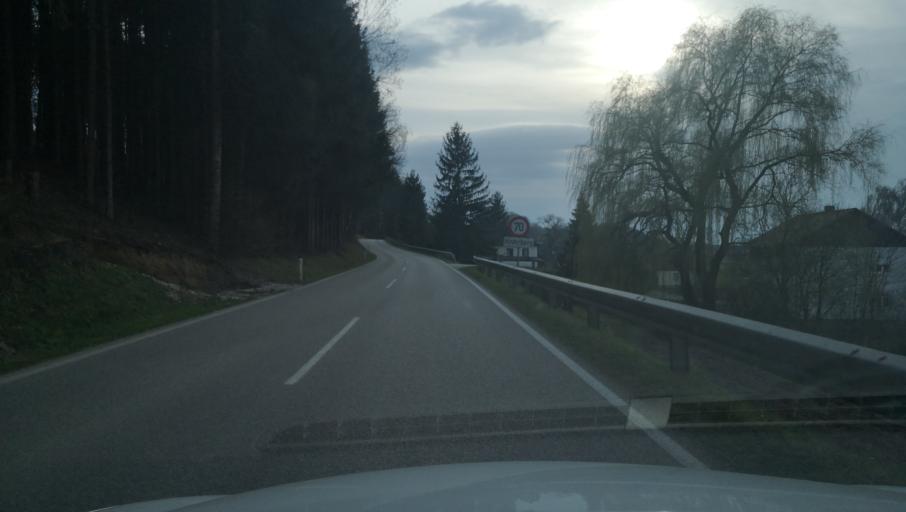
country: AT
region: Lower Austria
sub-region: Politischer Bezirk Amstetten
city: Amstetten
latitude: 48.0984
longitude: 14.8713
